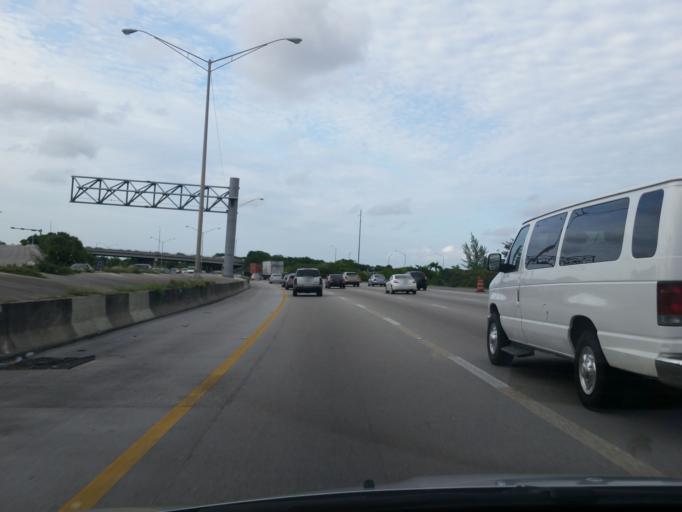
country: US
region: Florida
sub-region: Miami-Dade County
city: Ives Estates
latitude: 25.9612
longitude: -80.1671
